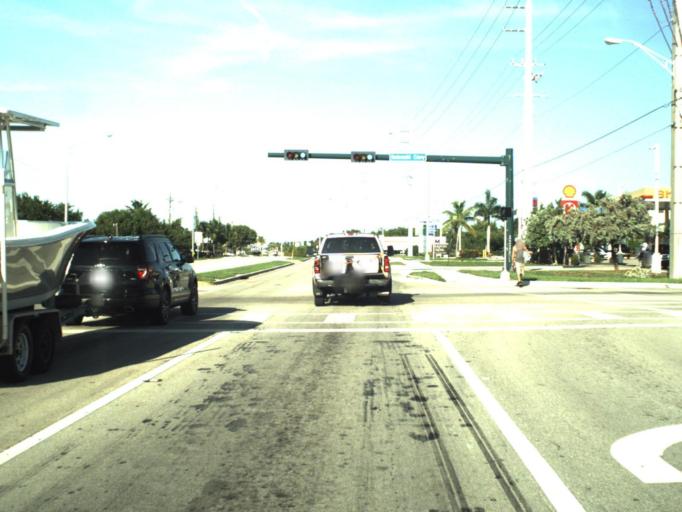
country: US
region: Florida
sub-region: Monroe County
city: Marathon
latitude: 24.7321
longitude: -81.0208
